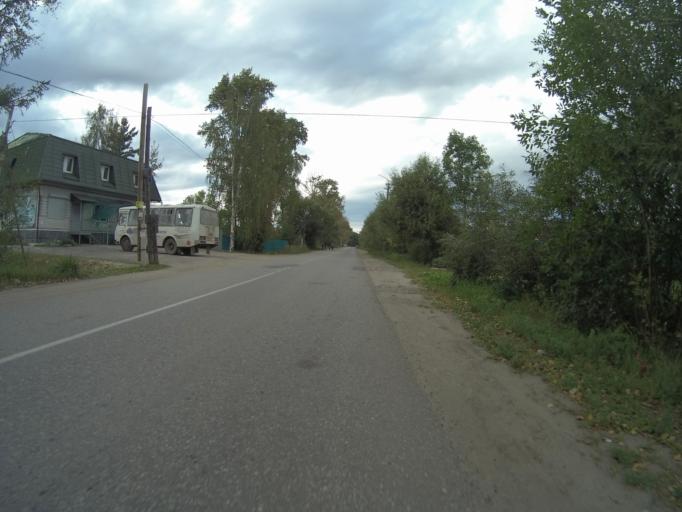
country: RU
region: Vladimir
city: Golovino
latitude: 55.9587
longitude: 40.4301
